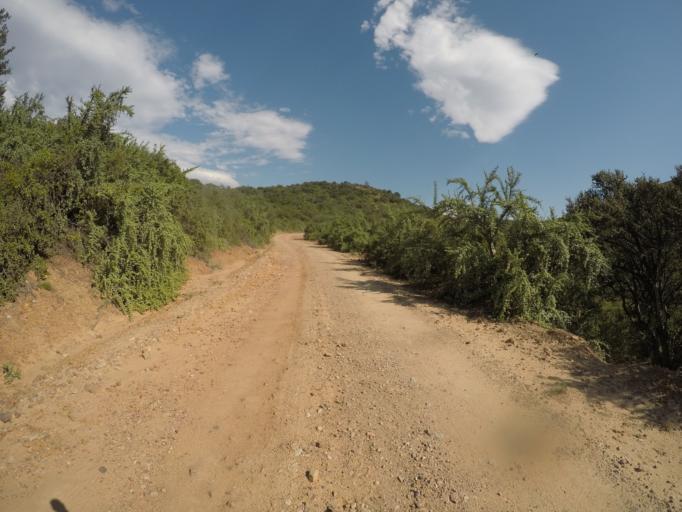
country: ZA
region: Eastern Cape
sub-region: Cacadu District Municipality
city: Kareedouw
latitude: -33.6552
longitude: 24.4090
